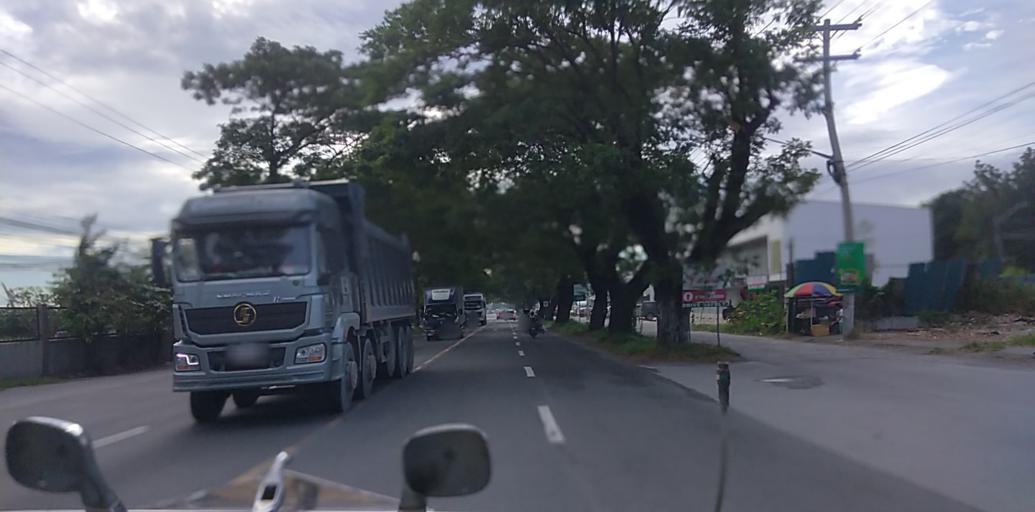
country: PH
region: Central Luzon
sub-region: Province of Pampanga
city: Telabastagan
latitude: 15.1044
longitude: 120.6174
